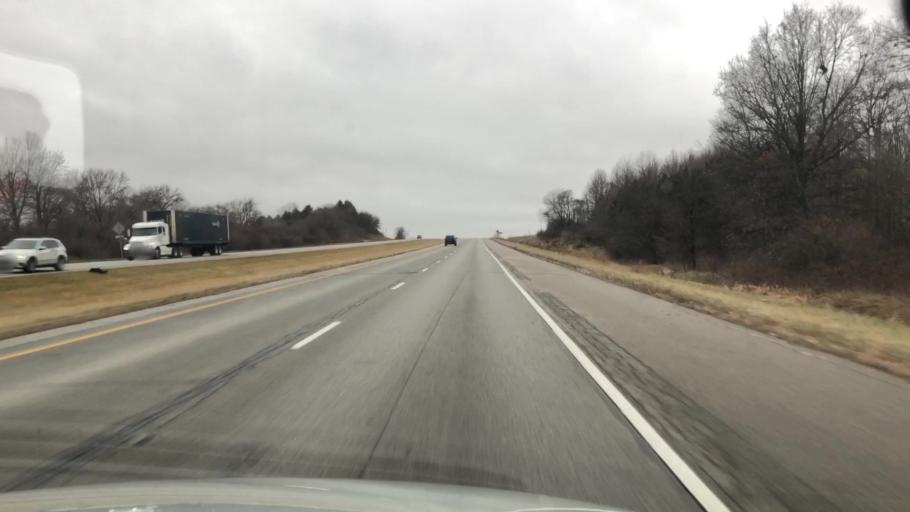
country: US
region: Indiana
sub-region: Kosciusko County
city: Mentone
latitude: 41.2651
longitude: -85.9720
